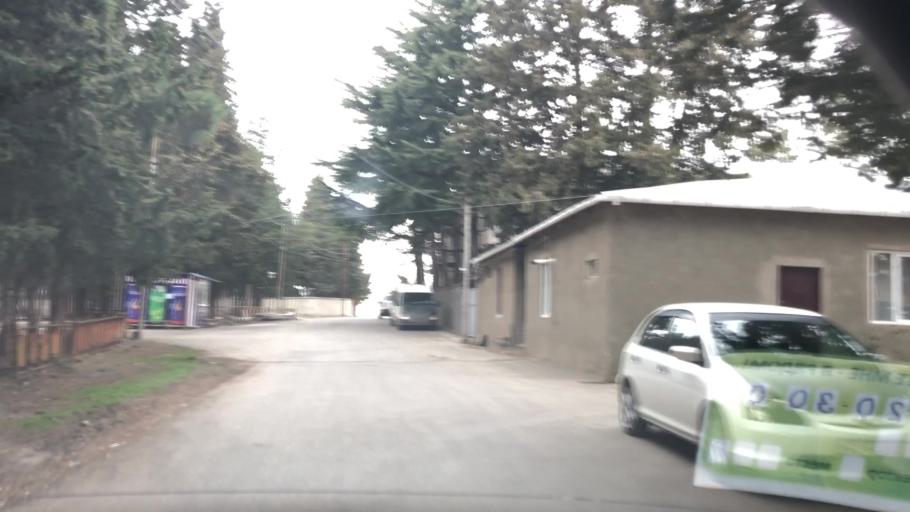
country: GE
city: Didi Lilo
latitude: 41.7029
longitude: 44.9289
